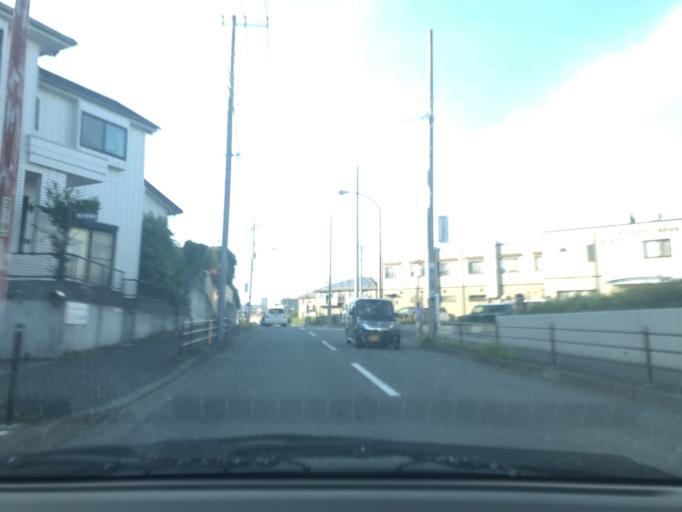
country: JP
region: Kanagawa
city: Fujisawa
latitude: 35.3419
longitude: 139.4627
